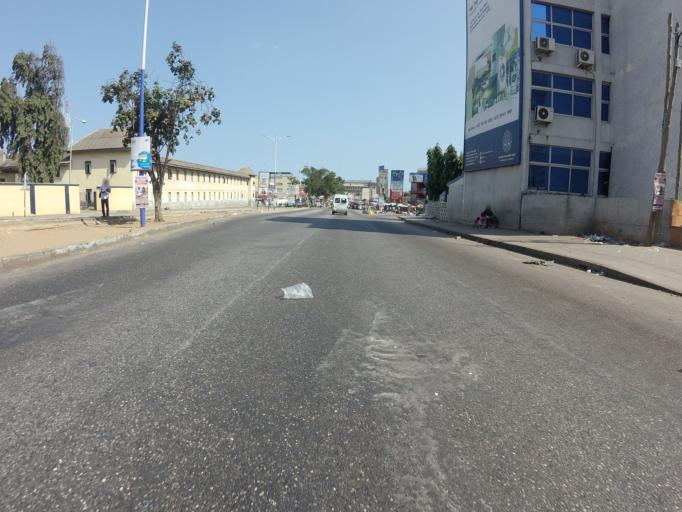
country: GH
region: Greater Accra
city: Accra
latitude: 5.5510
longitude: -0.2108
